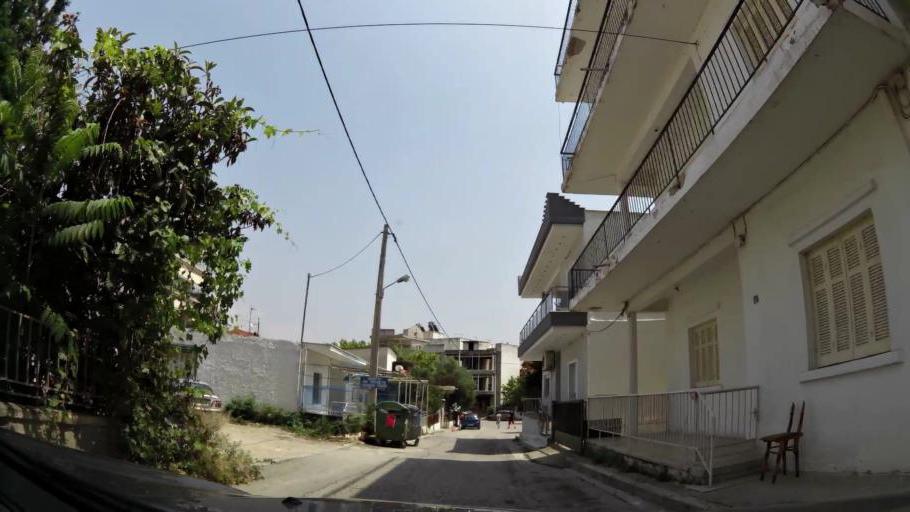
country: GR
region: Central Macedonia
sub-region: Nomos Thessalonikis
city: Evosmos
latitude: 40.6669
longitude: 22.9093
